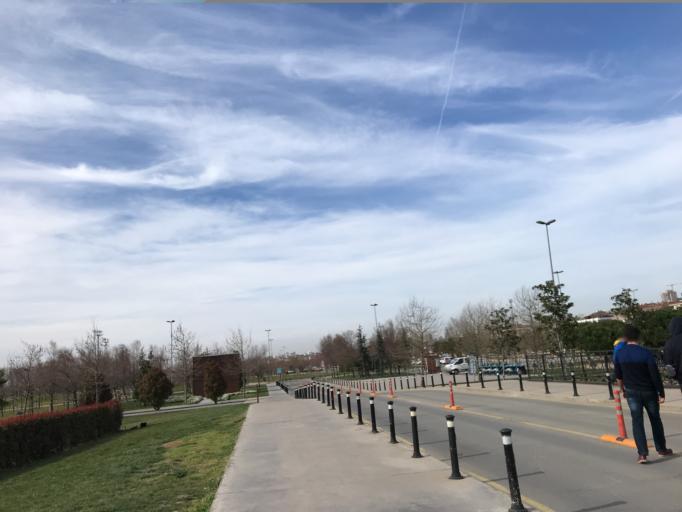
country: TR
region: Istanbul
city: Maltepe
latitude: 40.9329
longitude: 29.1158
